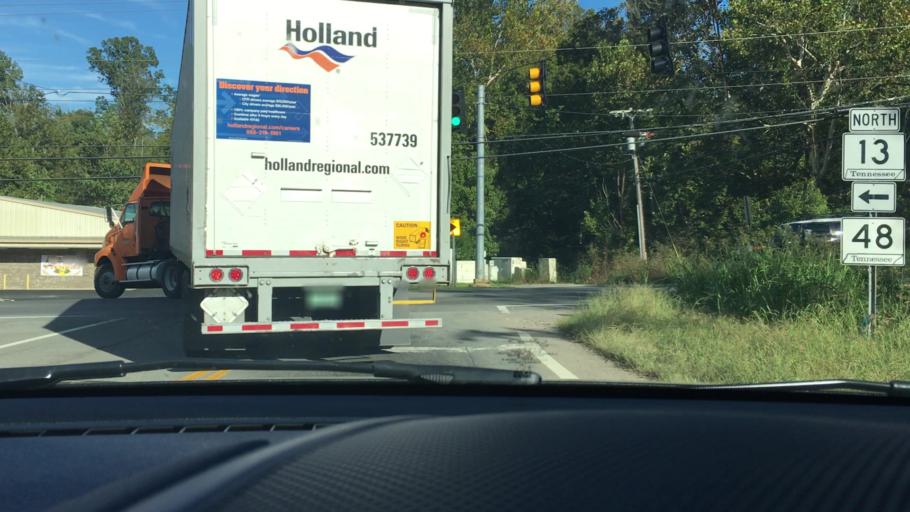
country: US
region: Tennessee
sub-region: Montgomery County
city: Clarksville
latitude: 36.4729
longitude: -87.3774
